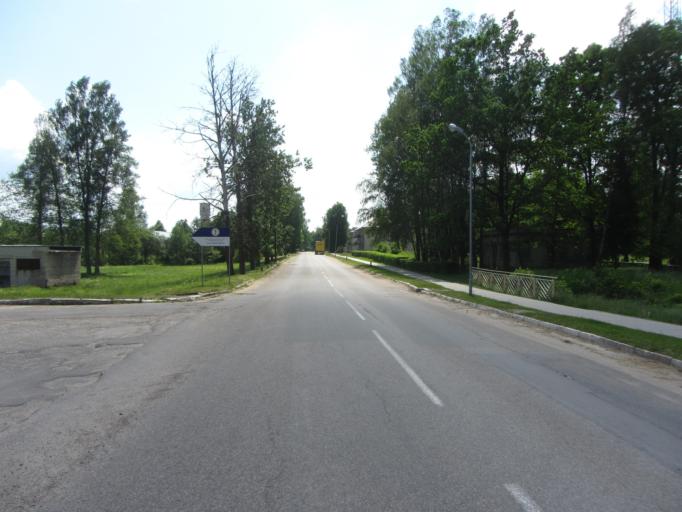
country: LT
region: Kauno apskritis
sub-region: Kauno rajonas
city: Karmelava
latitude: 54.9206
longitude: 24.2126
